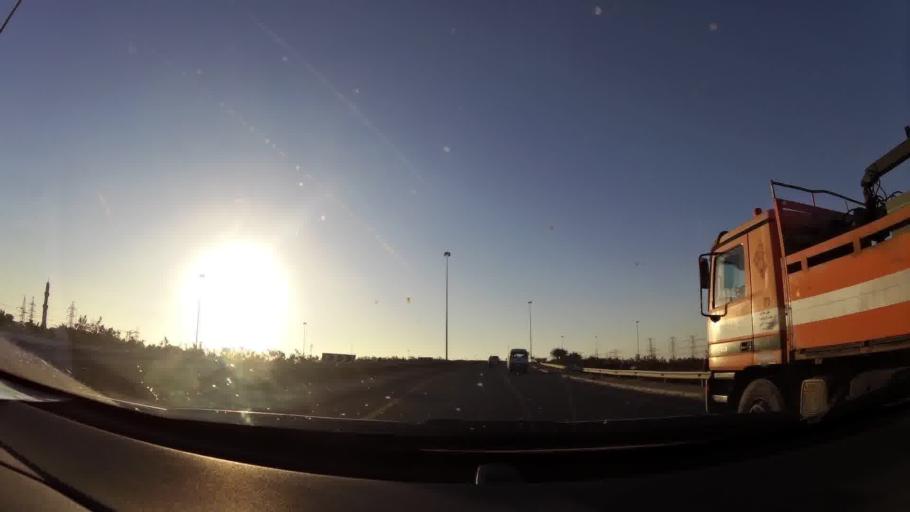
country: KW
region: Al Ahmadi
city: Al Fahahil
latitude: 28.9230
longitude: 48.2042
